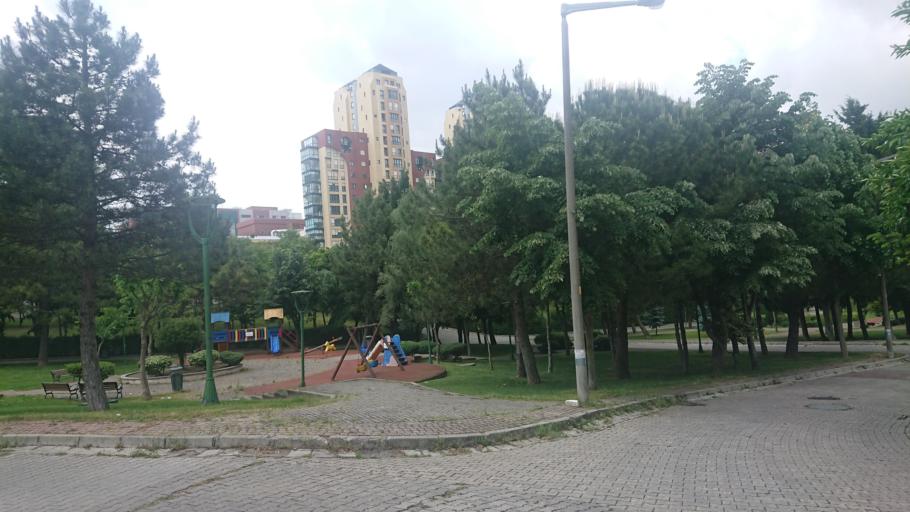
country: TR
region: Istanbul
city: Esenyurt
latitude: 41.0670
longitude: 28.6796
